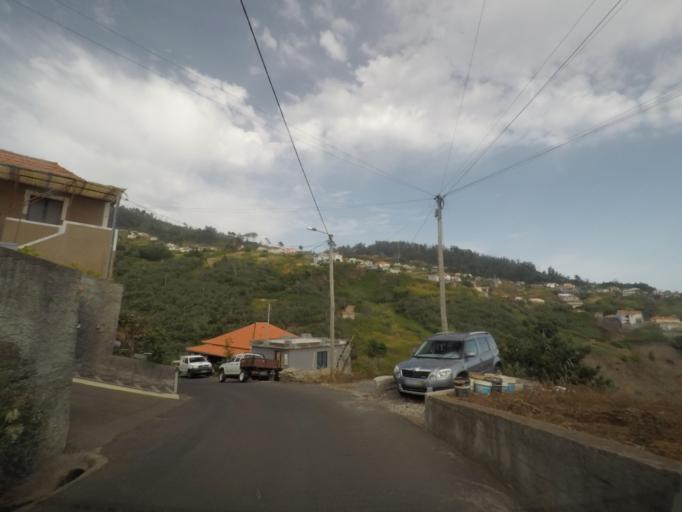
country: PT
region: Madeira
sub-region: Calheta
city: Arco da Calheta
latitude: 32.7320
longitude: -17.1539
